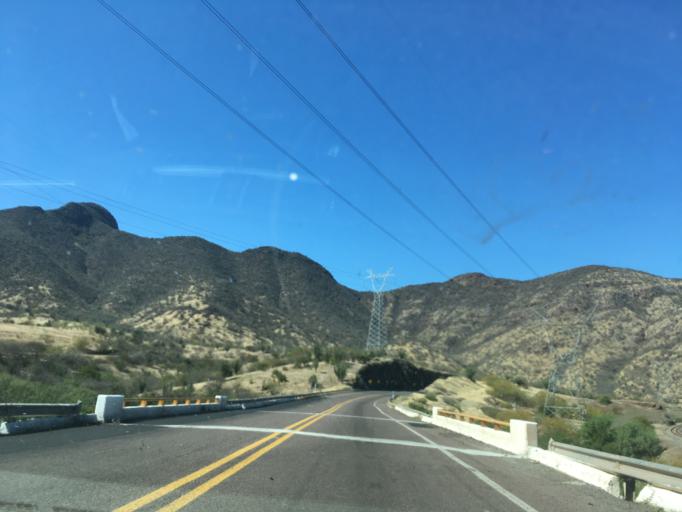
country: MX
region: Michoacan
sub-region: La Huacana
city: Cupuan del Rio
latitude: 18.7641
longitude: -102.0158
